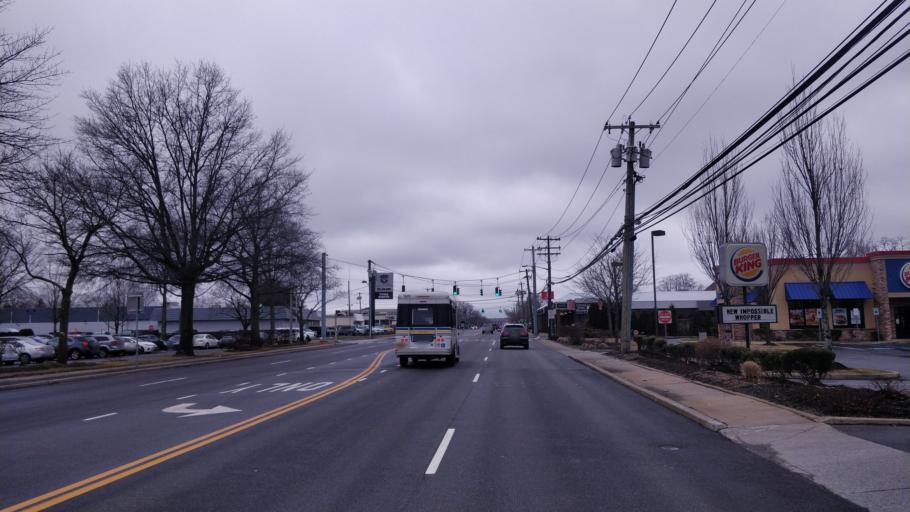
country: US
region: New York
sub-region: Suffolk County
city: Commack
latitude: 40.8414
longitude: -73.3073
